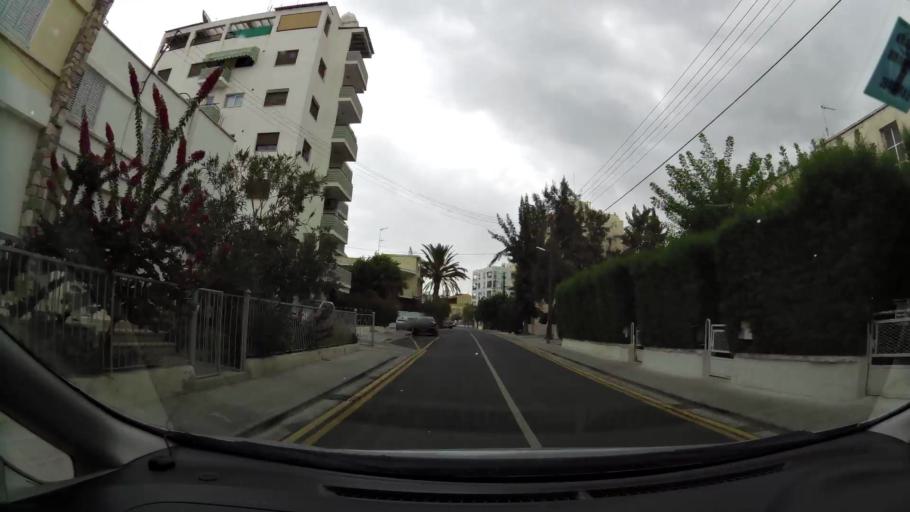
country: CY
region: Lefkosia
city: Nicosia
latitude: 35.1567
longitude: 33.3544
